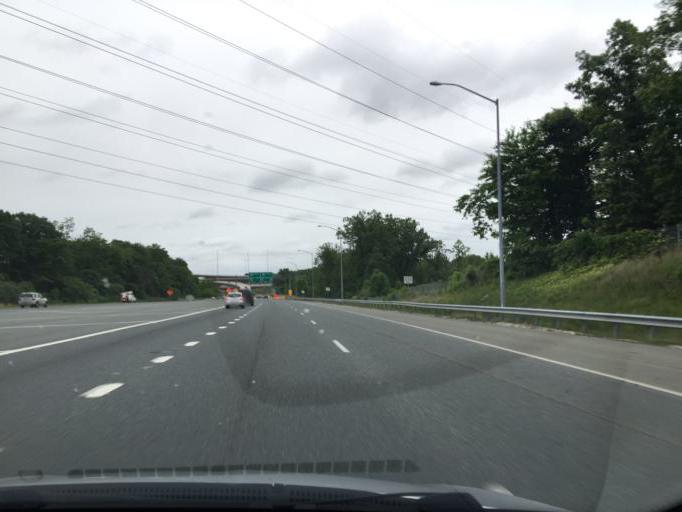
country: US
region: Maryland
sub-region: Baltimore County
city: Overlea
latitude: 39.3577
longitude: -76.5033
